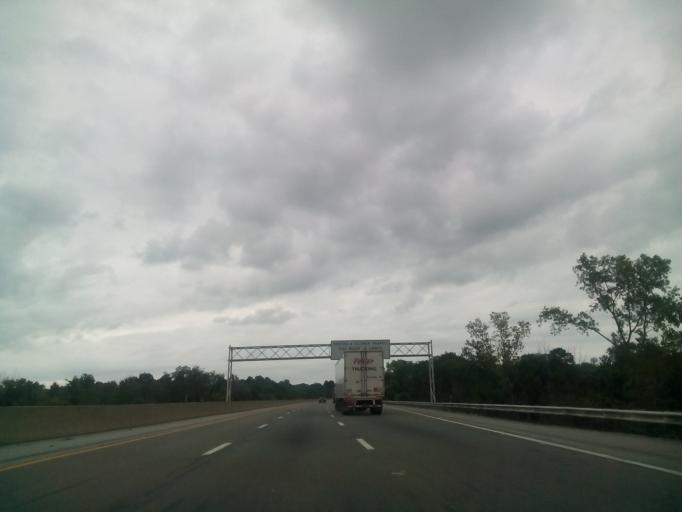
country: US
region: Ohio
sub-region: Erie County
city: Huron
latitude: 41.3282
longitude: -82.5035
